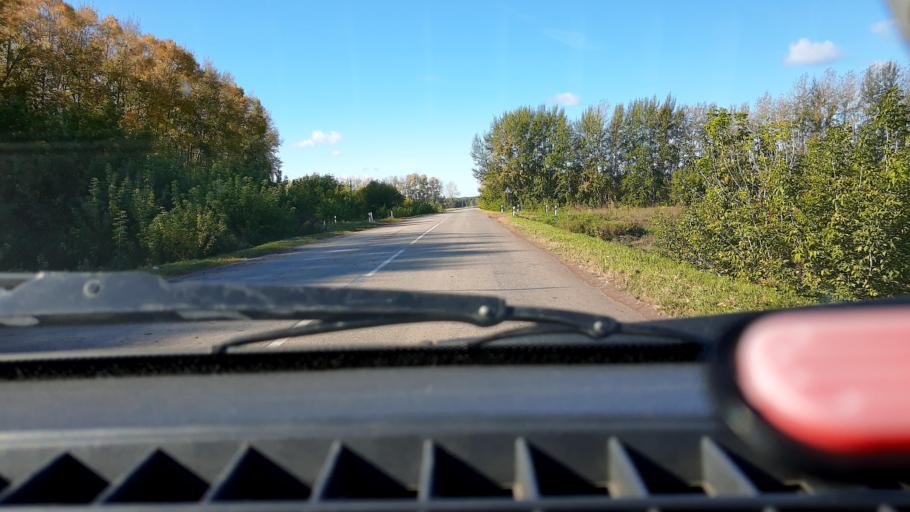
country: RU
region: Bashkortostan
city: Kushnarenkovo
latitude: 55.0609
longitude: 55.4372
